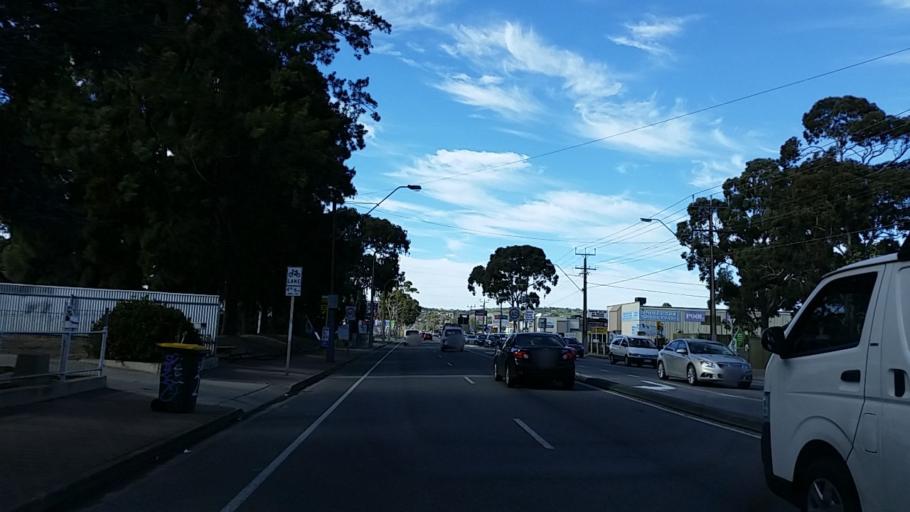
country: AU
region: South Australia
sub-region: Marion
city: Sturt
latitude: -35.0082
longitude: 138.5582
